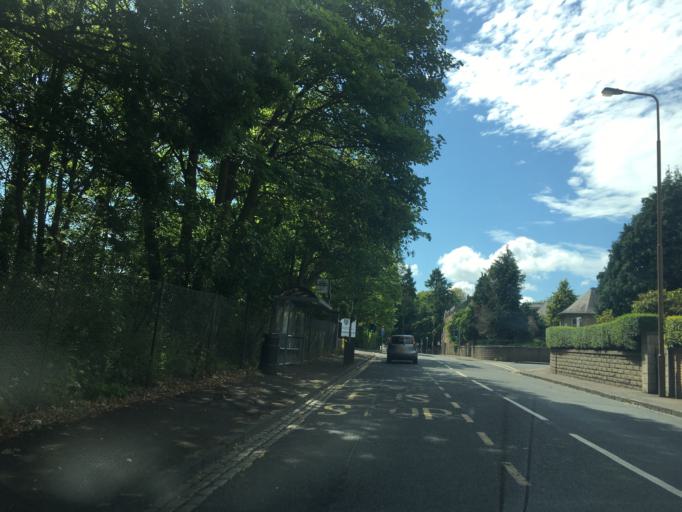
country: GB
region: Scotland
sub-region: West Lothian
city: Seafield
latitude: 55.9430
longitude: -3.1429
